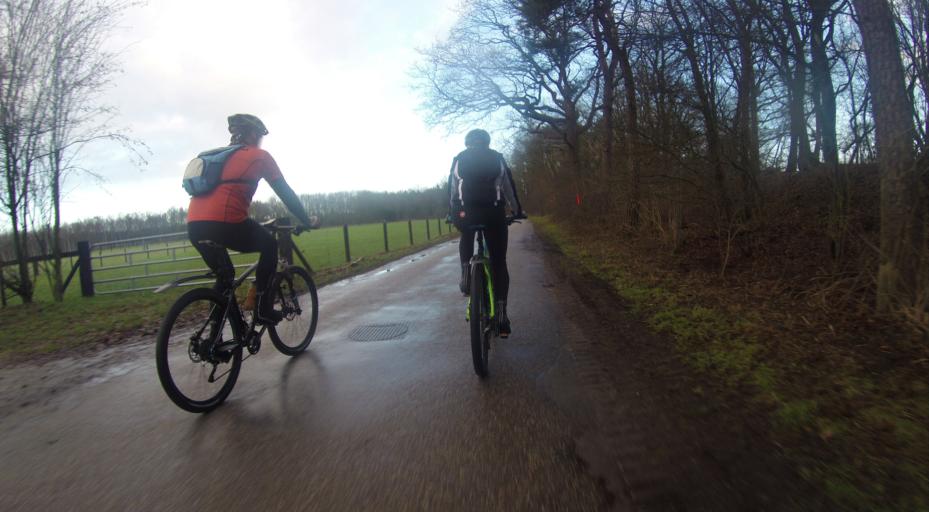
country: NL
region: Overijssel
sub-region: Gemeente Hof van Twente
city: Markelo
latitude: 52.2891
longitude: 6.4353
